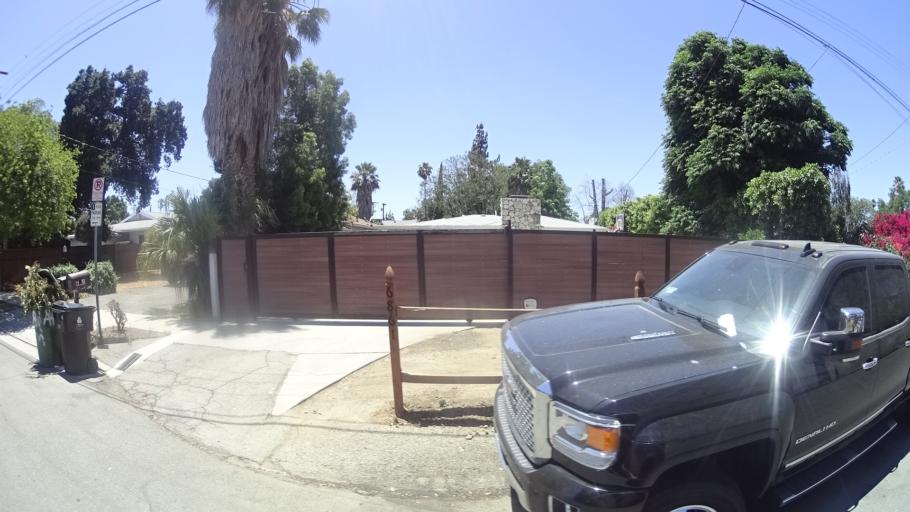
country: US
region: California
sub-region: Los Angeles County
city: Van Nuys
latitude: 34.1957
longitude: -118.4684
